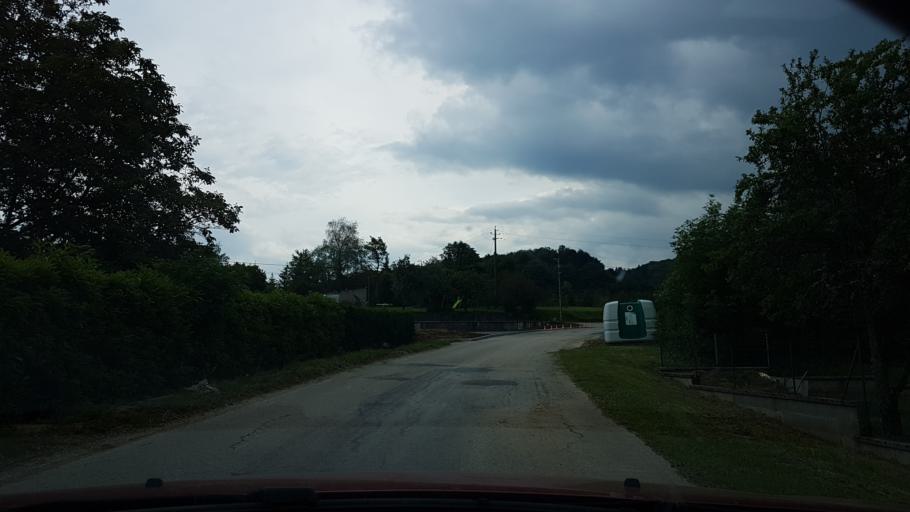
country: FR
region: Franche-Comte
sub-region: Departement du Jura
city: Orgelet
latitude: 46.5551
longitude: 5.6741
